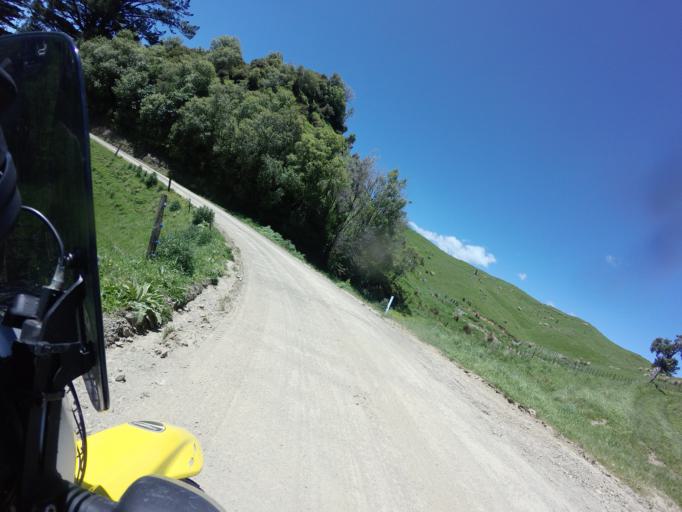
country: NZ
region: Bay of Plenty
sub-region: Opotiki District
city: Opotiki
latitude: -38.4049
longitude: 177.4524
